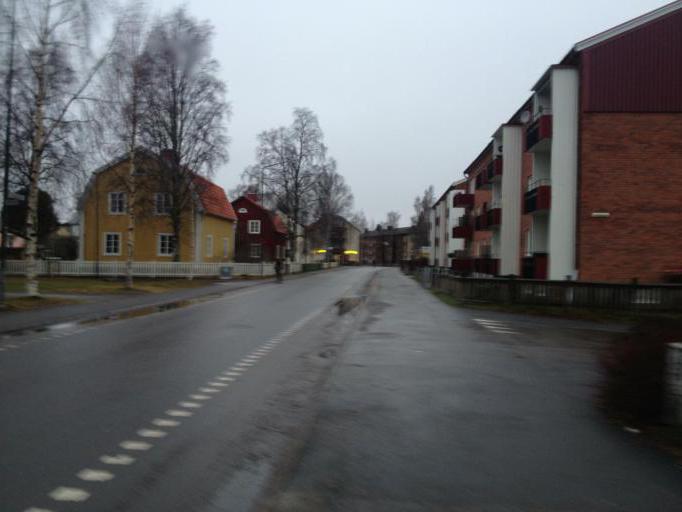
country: SE
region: Vaesterbotten
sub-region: Umea Kommun
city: Umea
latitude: 63.8212
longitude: 20.2867
